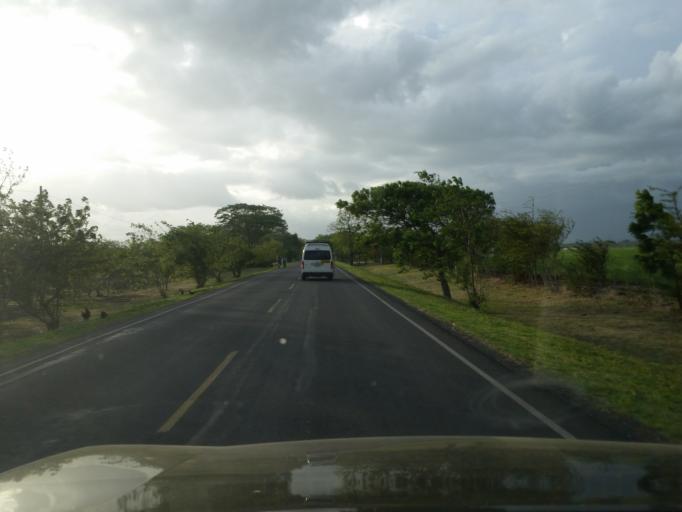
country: NI
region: Granada
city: Nandaime
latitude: 11.6825
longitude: -85.9871
